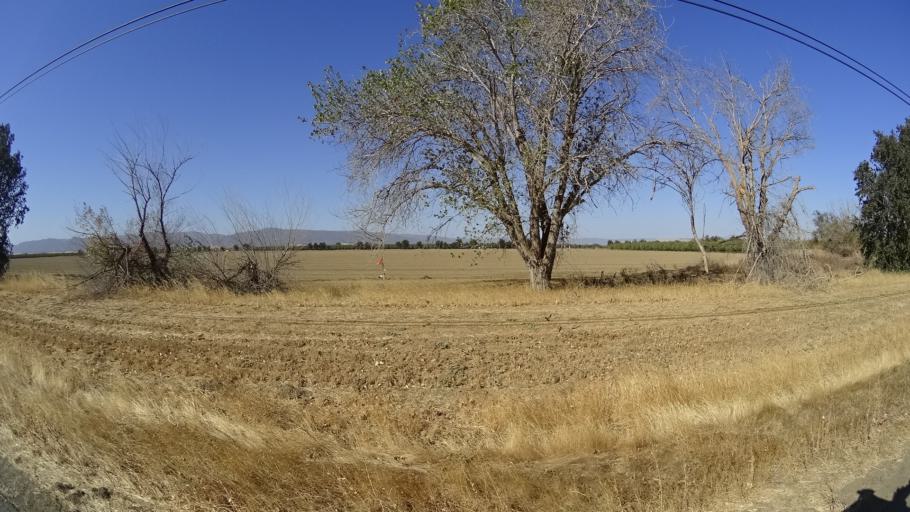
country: US
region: California
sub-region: Yolo County
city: Cottonwood
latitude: 38.6699
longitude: -121.9701
